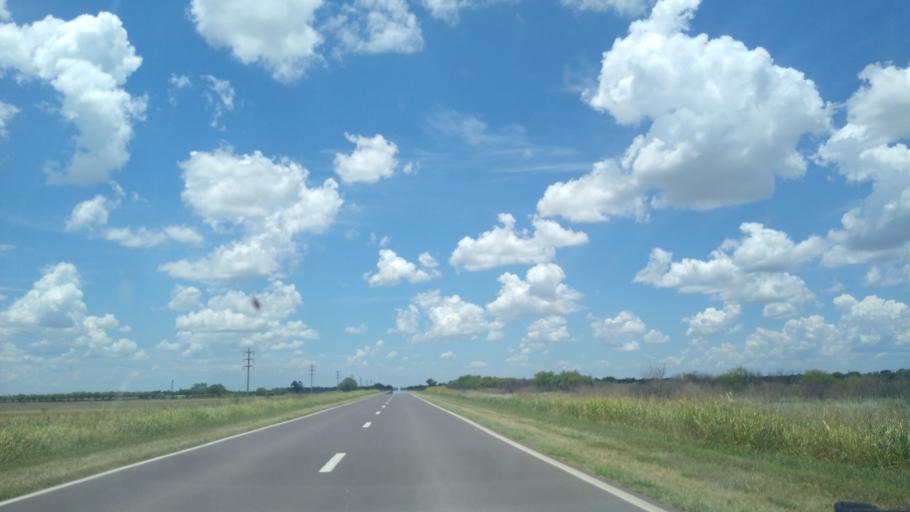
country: AR
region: Chaco
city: Presidencia Roque Saenz Pena
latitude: -26.7331
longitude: -60.3835
